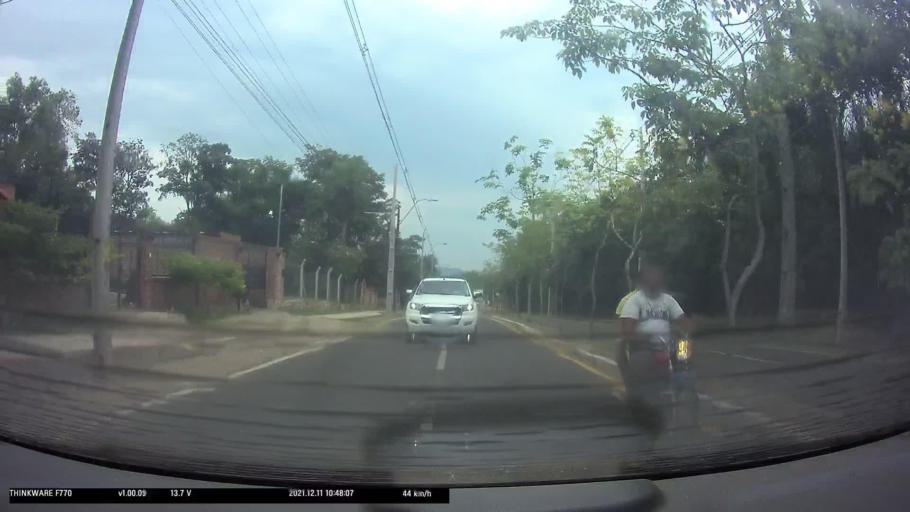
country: PY
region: Cordillera
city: San Bernardino
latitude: -25.3013
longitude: -57.2898
